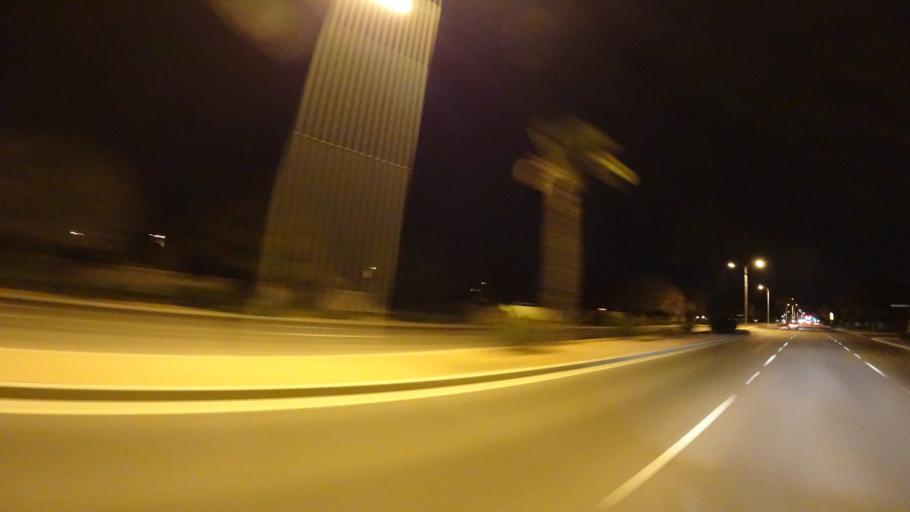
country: US
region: Arizona
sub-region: Maricopa County
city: San Carlos
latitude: 33.3206
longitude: -111.8686
